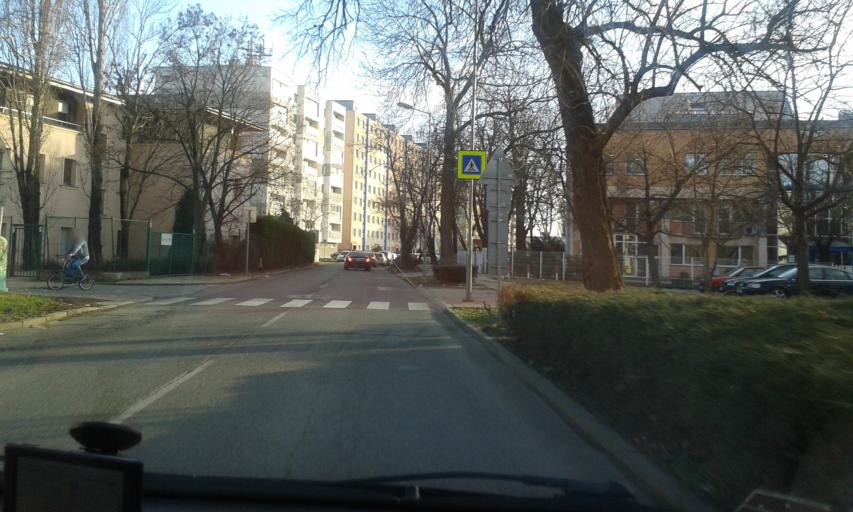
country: SK
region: Bratislavsky
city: Bratislava
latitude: 48.1845
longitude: 17.1367
